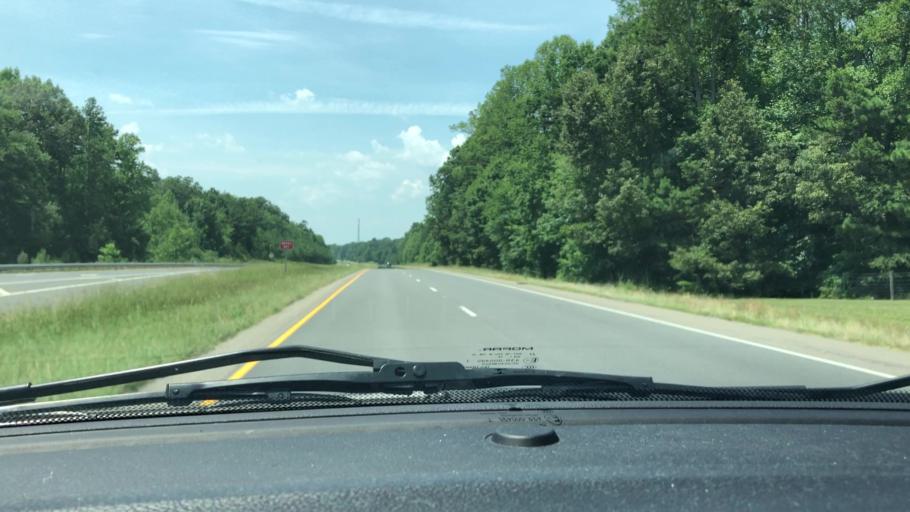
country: US
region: North Carolina
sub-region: Chatham County
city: Siler City
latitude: 35.6376
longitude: -79.3747
